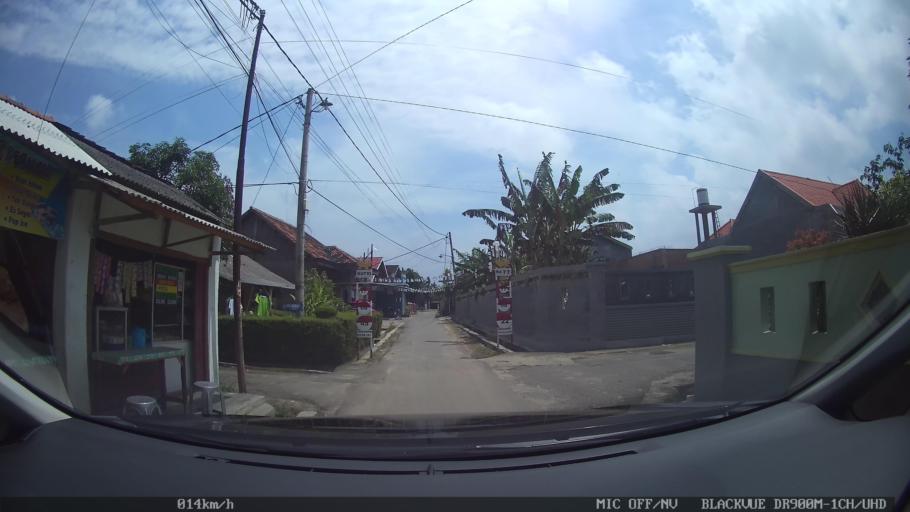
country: ID
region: Lampung
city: Kedaton
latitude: -5.3723
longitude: 105.3056
